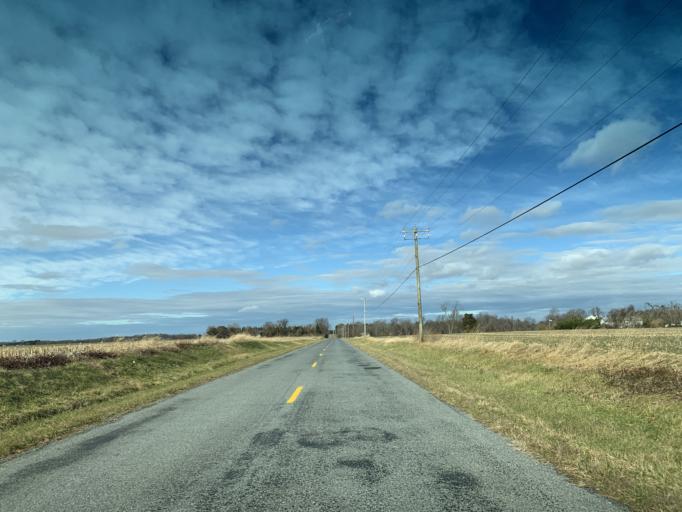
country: US
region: Maryland
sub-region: Kent County
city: Chestertown
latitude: 39.3324
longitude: -76.0446
